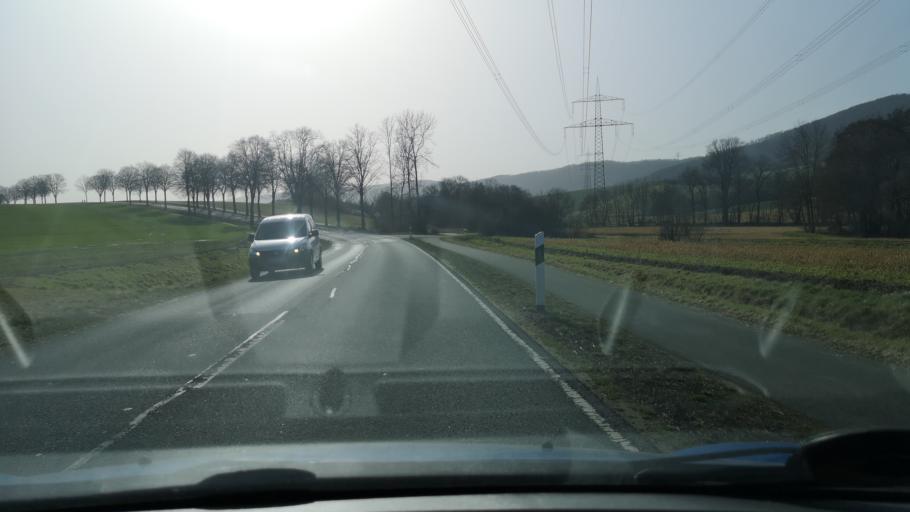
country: DE
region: Lower Saxony
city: Salzhemmendorf
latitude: 52.0457
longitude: 9.5966
